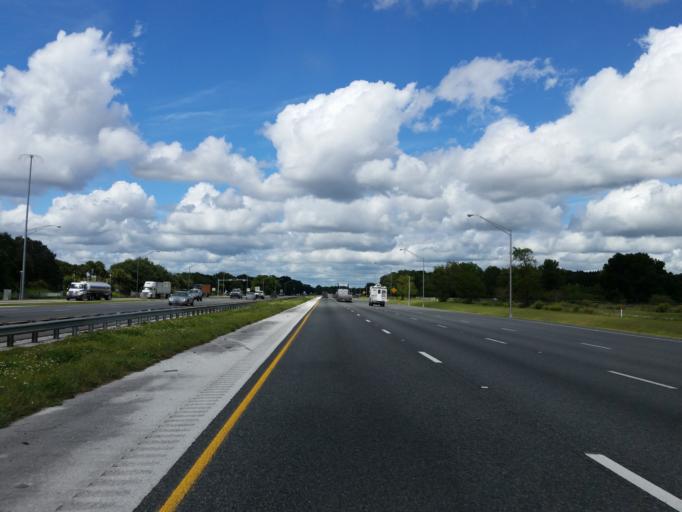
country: US
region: Florida
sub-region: Marion County
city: Belleview
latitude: 28.9974
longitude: -82.1459
